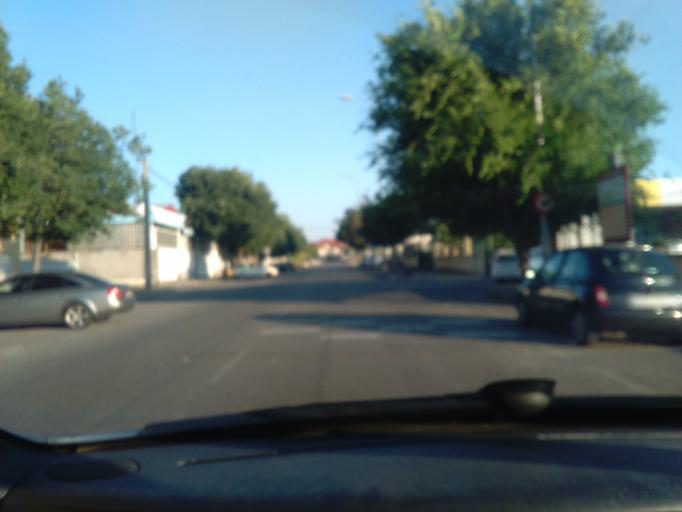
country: ES
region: Andalusia
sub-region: Provincia de Sevilla
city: Sevilla
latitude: 37.3947
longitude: -5.9469
